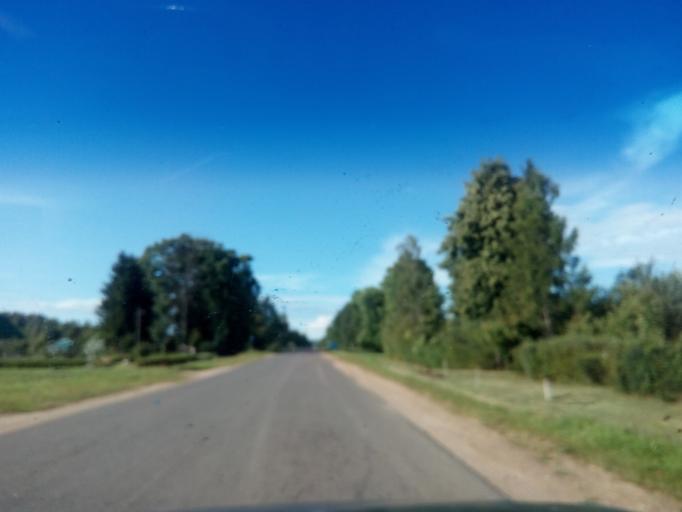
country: BY
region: Vitebsk
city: Dzisna
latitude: 55.6560
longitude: 28.3226
